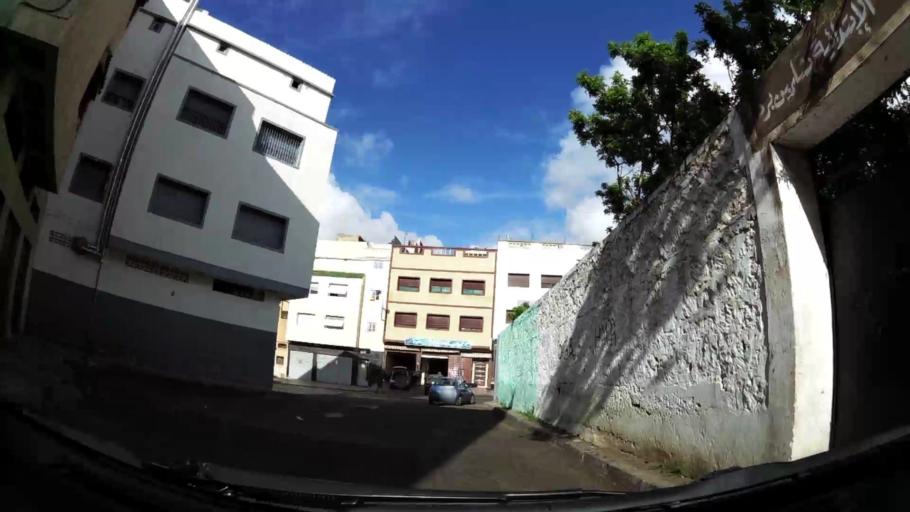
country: MA
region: Grand Casablanca
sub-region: Casablanca
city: Casablanca
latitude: 33.5444
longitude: -7.5977
